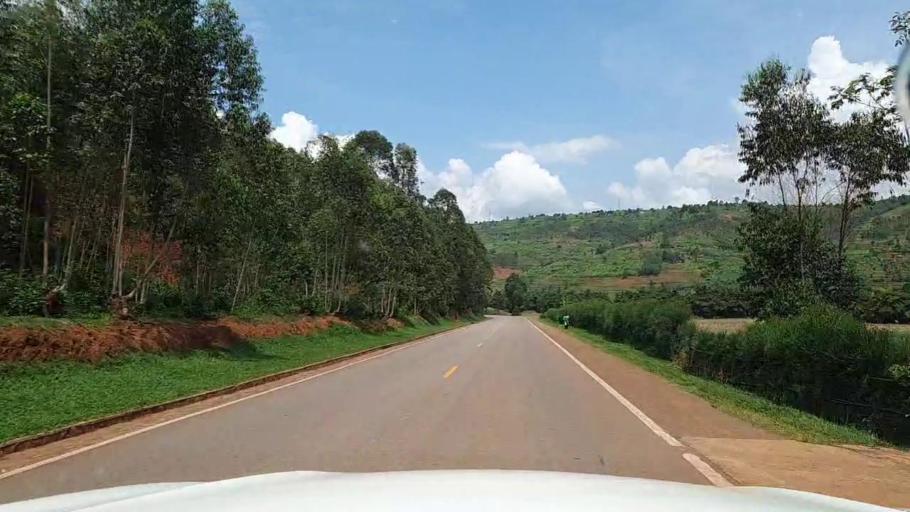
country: RW
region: Kigali
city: Kigali
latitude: -1.8467
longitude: 30.0954
